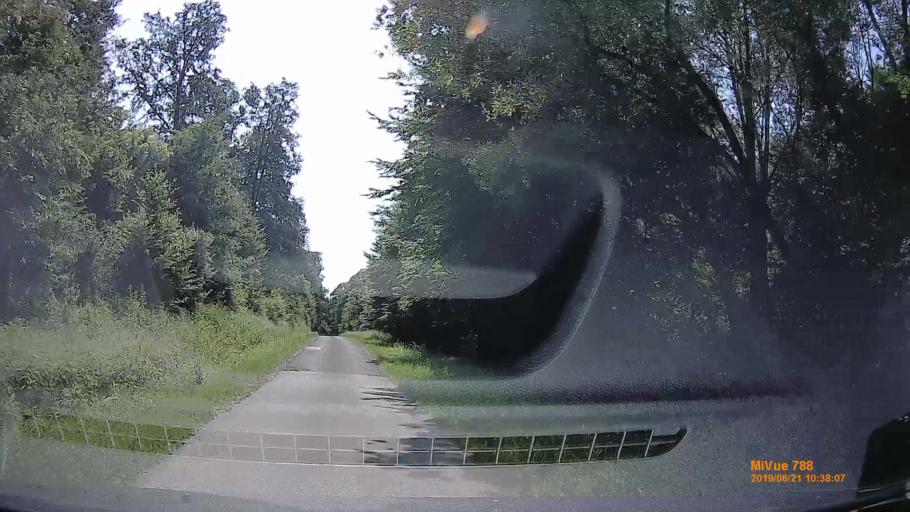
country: HU
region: Baranya
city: Buekkoesd
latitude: 46.1368
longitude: 17.9790
